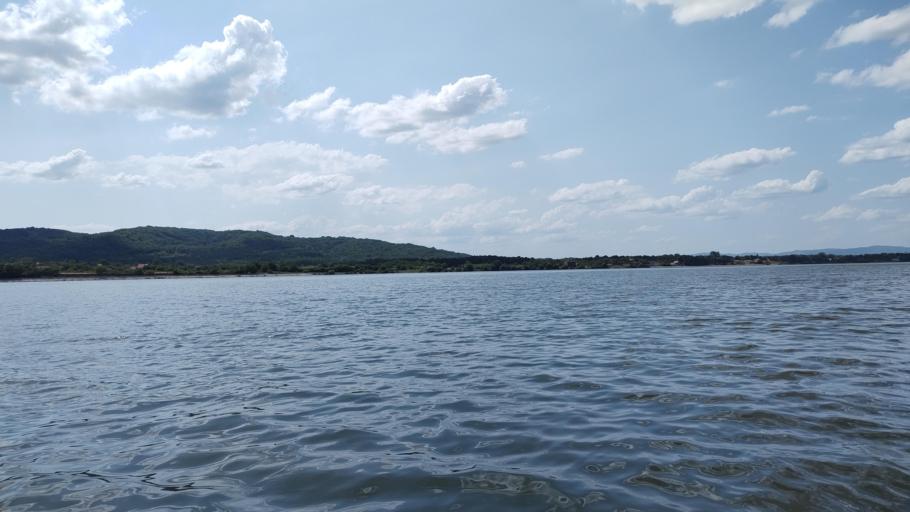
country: RS
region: Central Serbia
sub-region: Branicevski Okrug
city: Golubac
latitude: 44.6695
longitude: 21.6198
